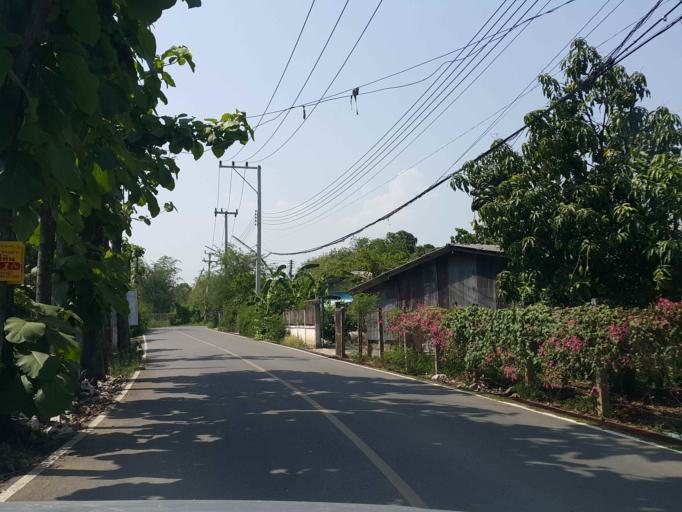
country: TH
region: Chiang Mai
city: San Kamphaeng
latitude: 18.7811
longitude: 99.1300
